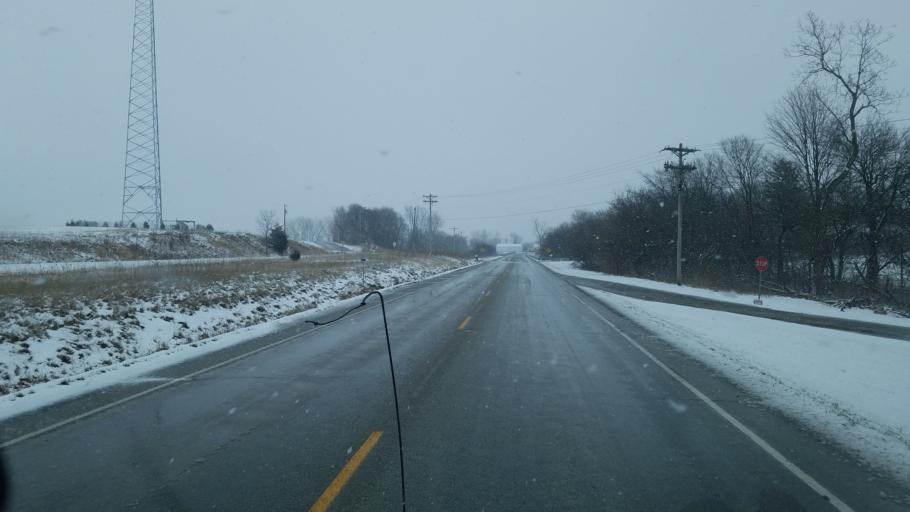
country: US
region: Indiana
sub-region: Randolph County
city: Lynn
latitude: 39.9689
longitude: -85.0334
